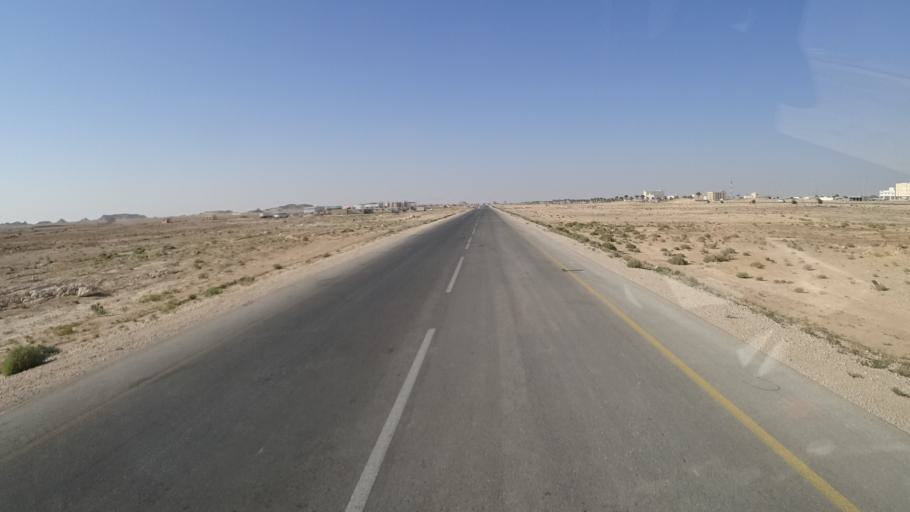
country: OM
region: Zufar
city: Salalah
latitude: 17.6005
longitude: 54.0350
